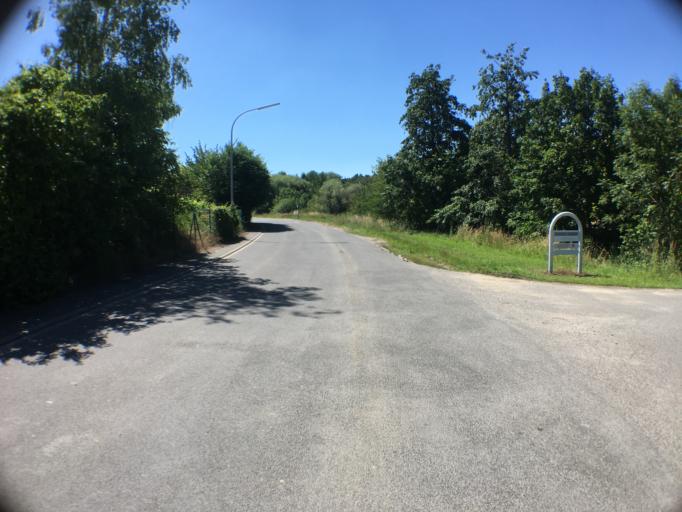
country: DE
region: Bavaria
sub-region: Regierungsbezirk Unterfranken
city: Wiesentheid
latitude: 49.7846
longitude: 10.3358
